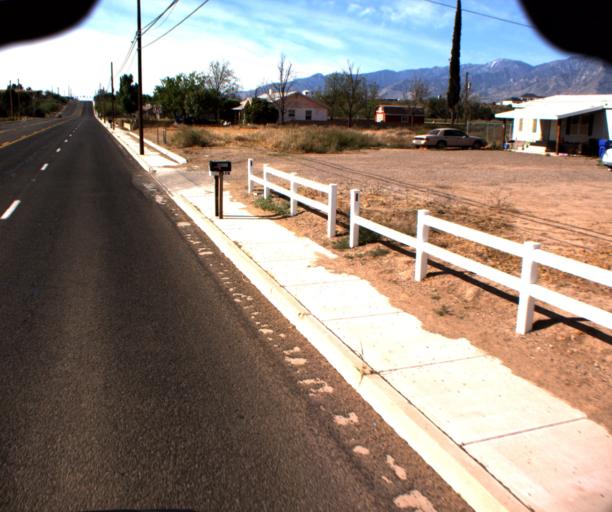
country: US
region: Arizona
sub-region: Graham County
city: Safford
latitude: 32.8098
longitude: -109.7078
